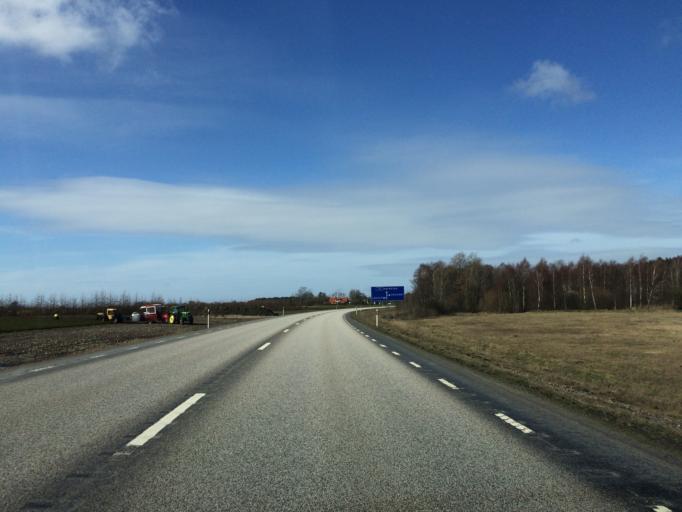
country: SE
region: Halland
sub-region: Laholms Kommun
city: Veinge
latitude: 56.5277
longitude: 13.1754
